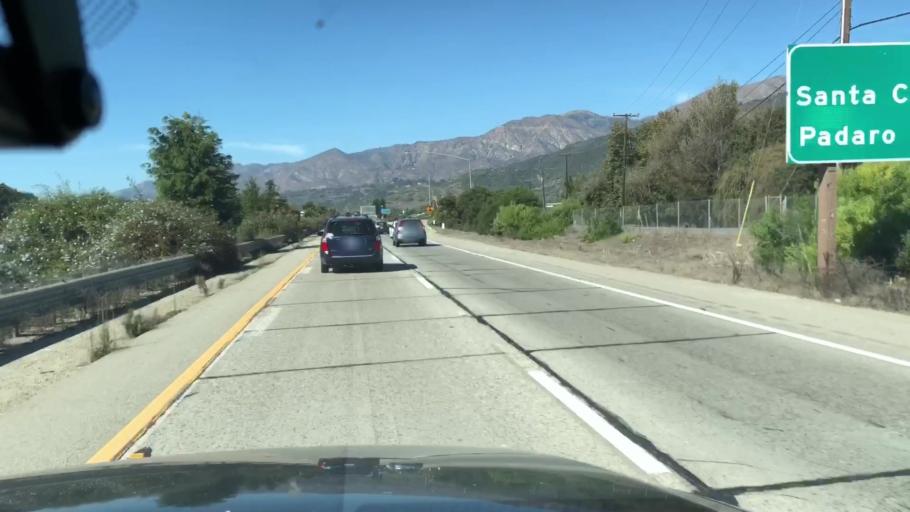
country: US
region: California
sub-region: Santa Barbara County
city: Toro Canyon
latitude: 34.4079
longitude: -119.5488
